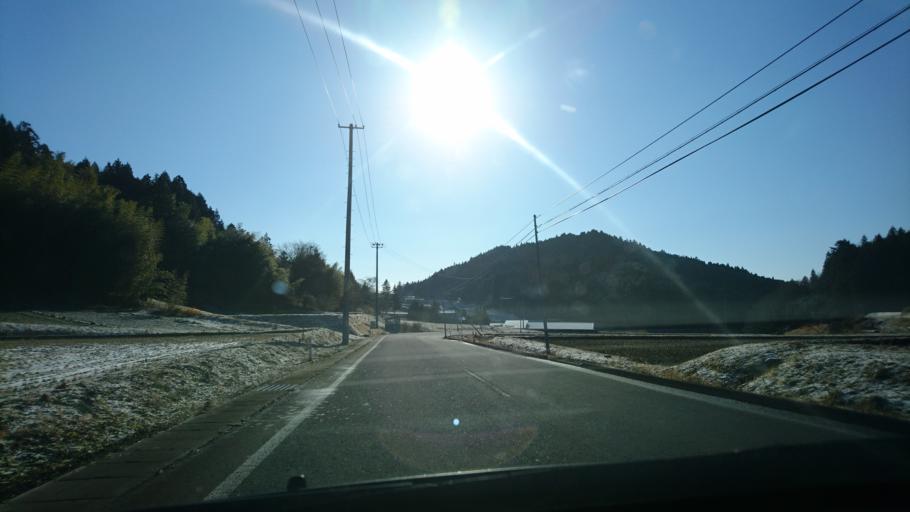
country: JP
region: Iwate
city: Ichinoseki
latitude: 38.8796
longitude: 141.3189
